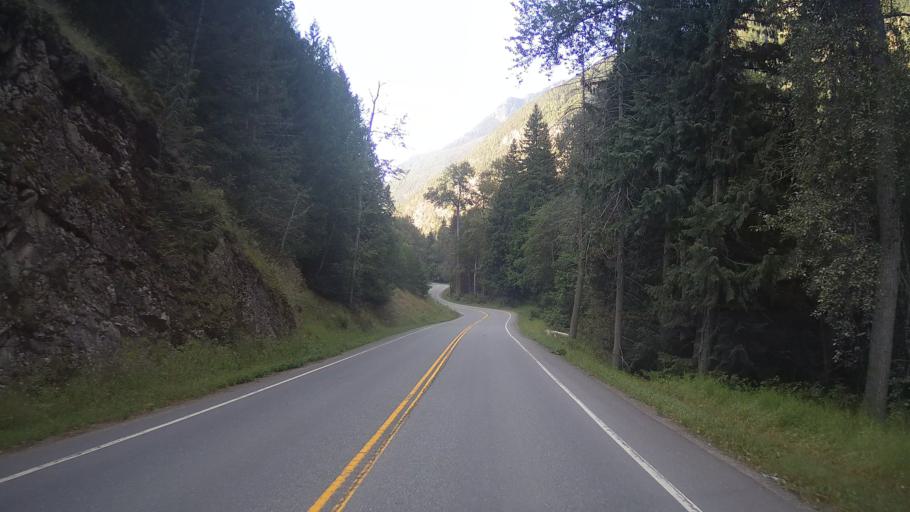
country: CA
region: British Columbia
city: Lillooet
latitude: 50.6208
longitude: -122.1030
